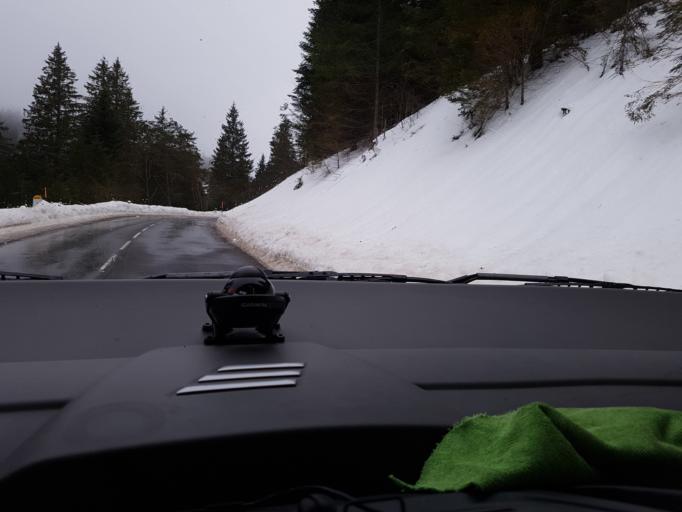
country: FR
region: Alsace
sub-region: Departement du Haut-Rhin
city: Soultzeren
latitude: 48.1286
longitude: 7.0919
